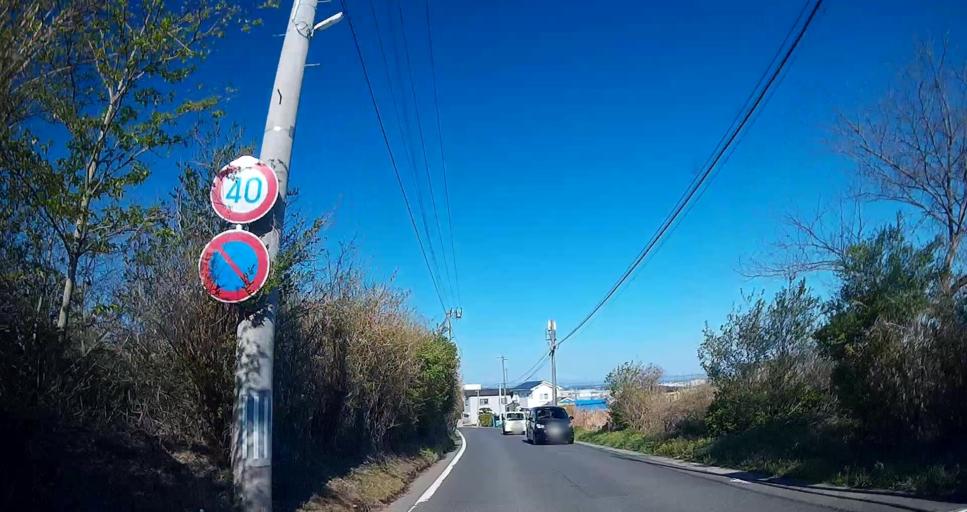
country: JP
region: Aomori
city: Hachinohe
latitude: 40.5224
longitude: 141.5617
